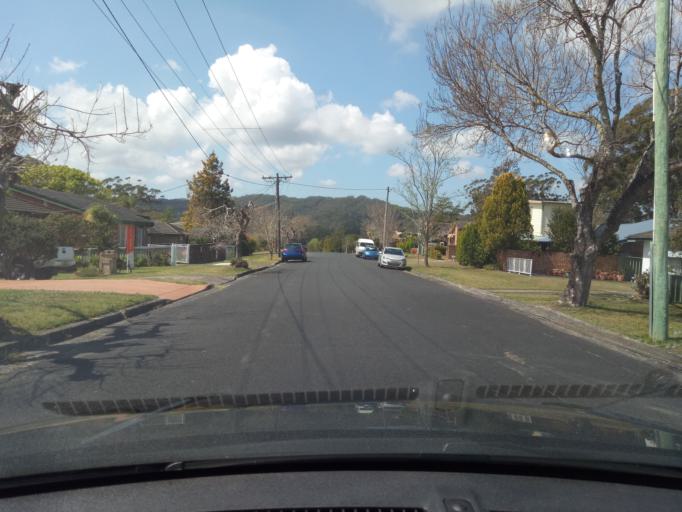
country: AU
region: New South Wales
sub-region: Gosford Shire
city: Narara
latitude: -33.3983
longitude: 151.3529
